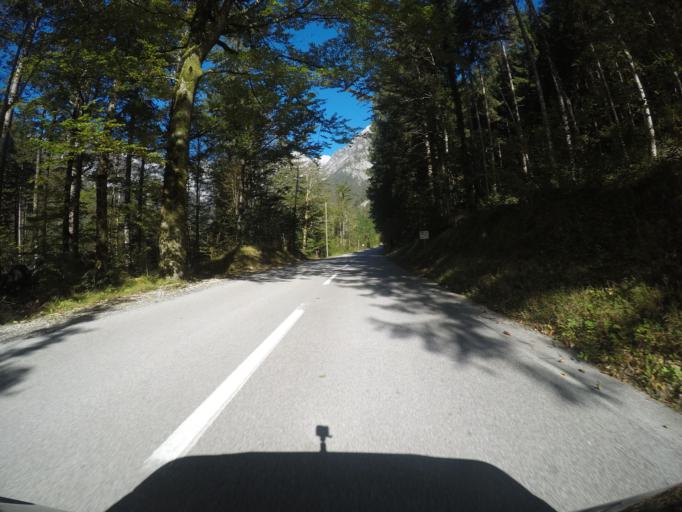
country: SI
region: Kamnik
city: Mekinje
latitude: 46.3220
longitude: 14.5941
